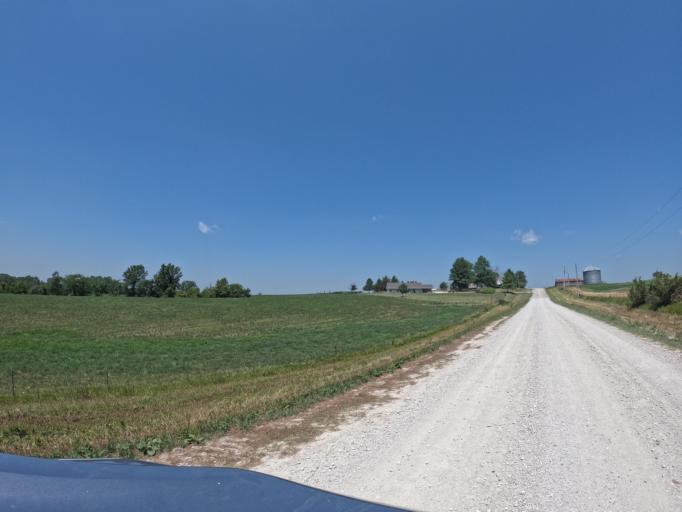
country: US
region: Iowa
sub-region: Keokuk County
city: Sigourney
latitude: 41.2589
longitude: -92.1697
